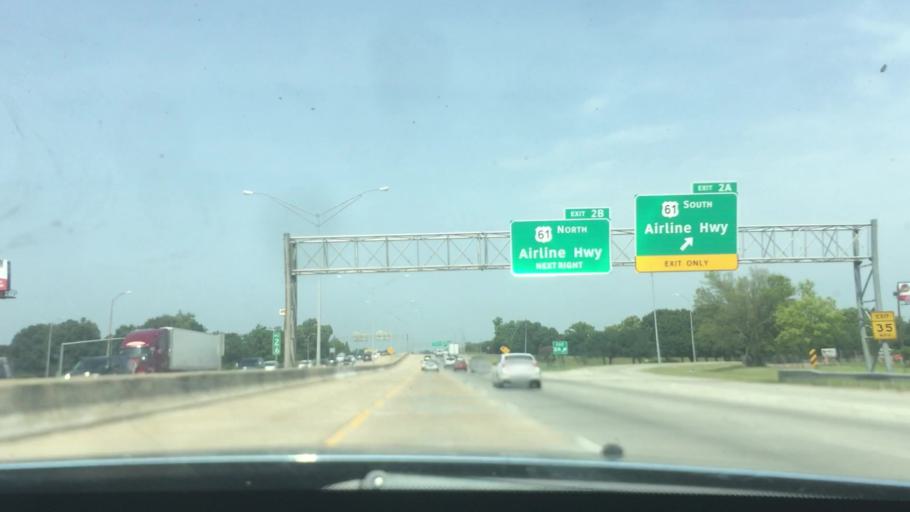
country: US
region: Louisiana
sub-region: East Baton Rouge Parish
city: Westminster
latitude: 30.4220
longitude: -91.0793
